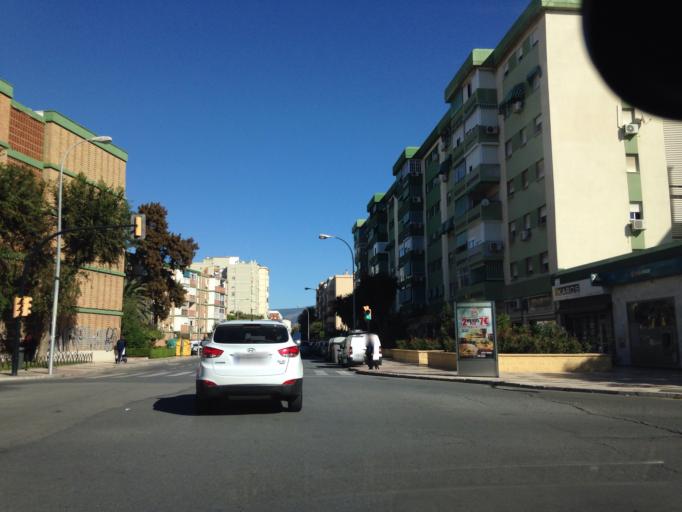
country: ES
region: Andalusia
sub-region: Provincia de Malaga
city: Malaga
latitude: 36.6895
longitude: -4.4512
